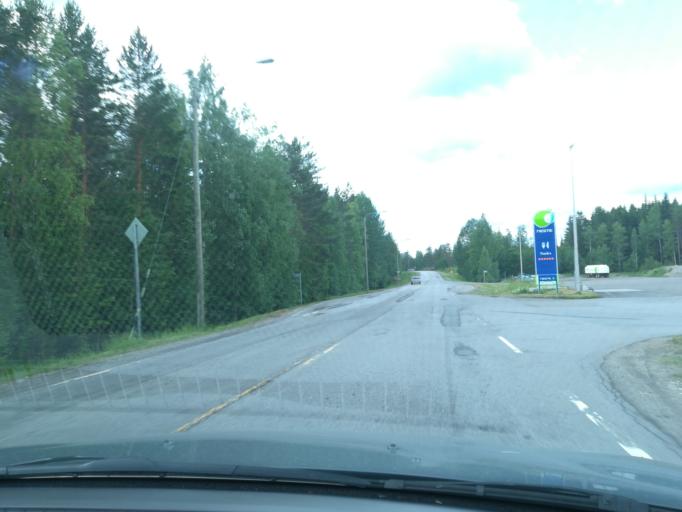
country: FI
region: Southern Savonia
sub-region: Mikkeli
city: Ristiina
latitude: 61.4529
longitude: 27.2639
